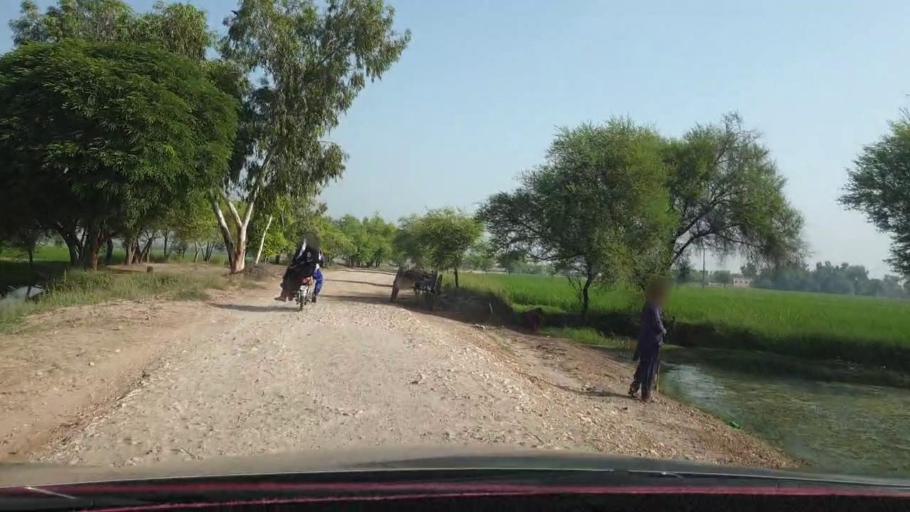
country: PK
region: Sindh
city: Nasirabad
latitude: 27.4577
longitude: 67.9179
